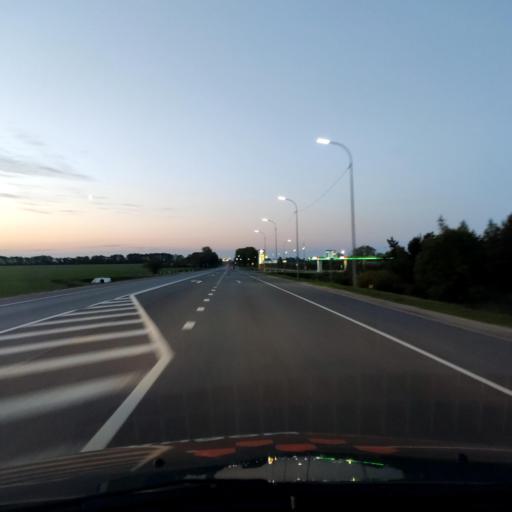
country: RU
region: Orjol
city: Zmiyevka
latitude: 52.7125
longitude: 36.3495
